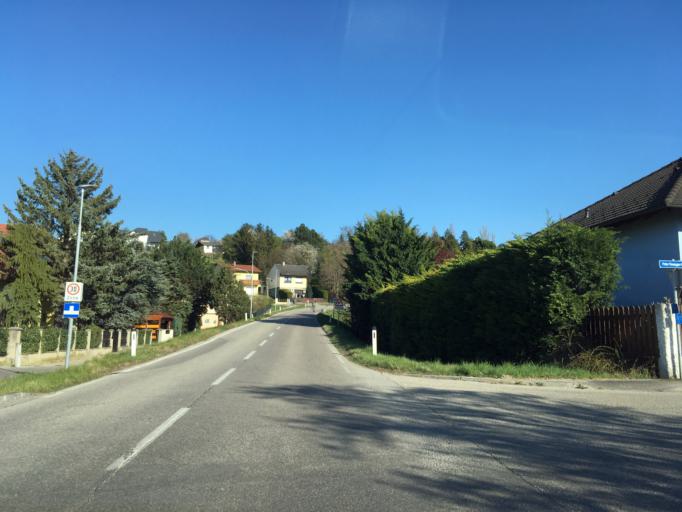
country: AT
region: Lower Austria
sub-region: Politischer Bezirk Tulln
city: Konigstetten
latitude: 48.3019
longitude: 16.1576
